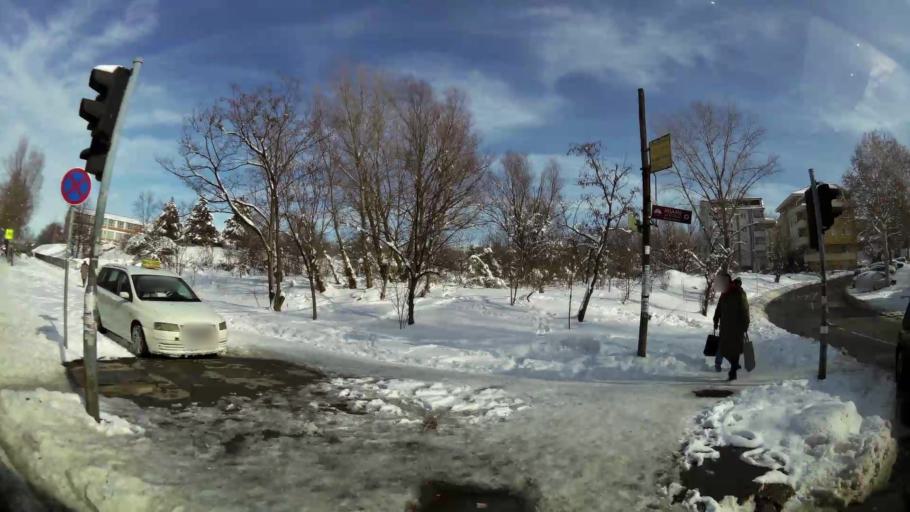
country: RS
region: Central Serbia
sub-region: Belgrade
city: Zvezdara
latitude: 44.7904
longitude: 20.5407
